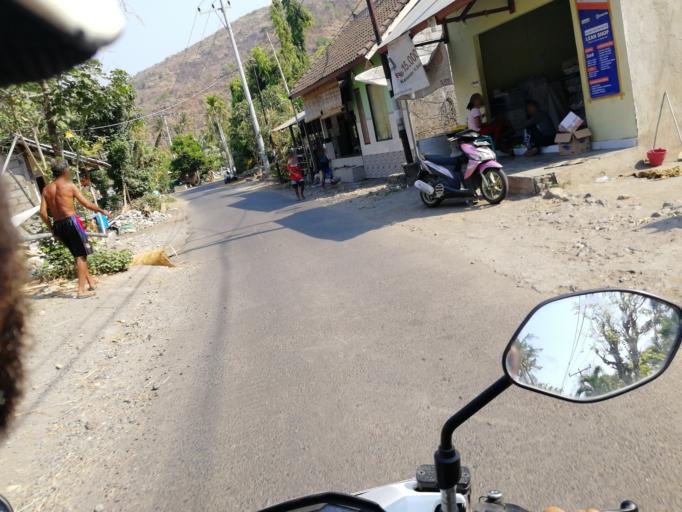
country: ID
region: Bali
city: Biaslantang Kaler
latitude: -8.3536
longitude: 115.6878
